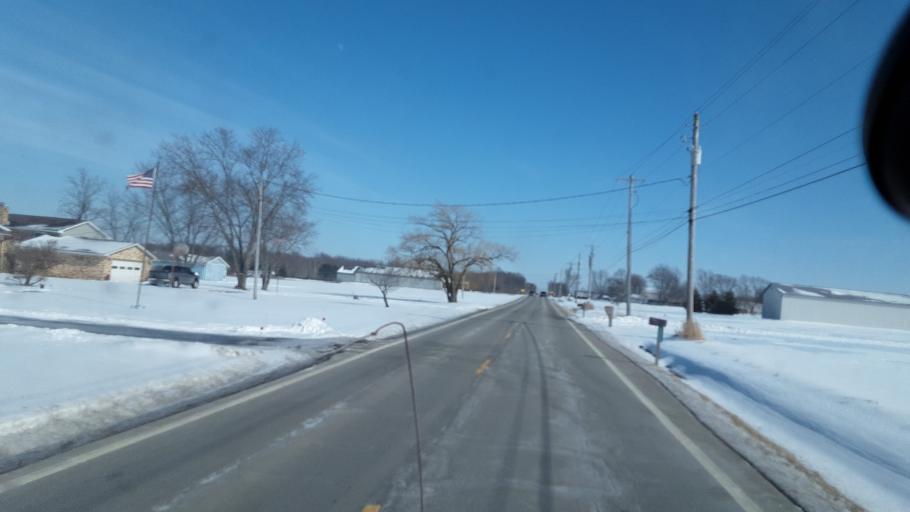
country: US
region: Ohio
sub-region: Columbiana County
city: Salem
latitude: 40.9445
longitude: -80.8627
